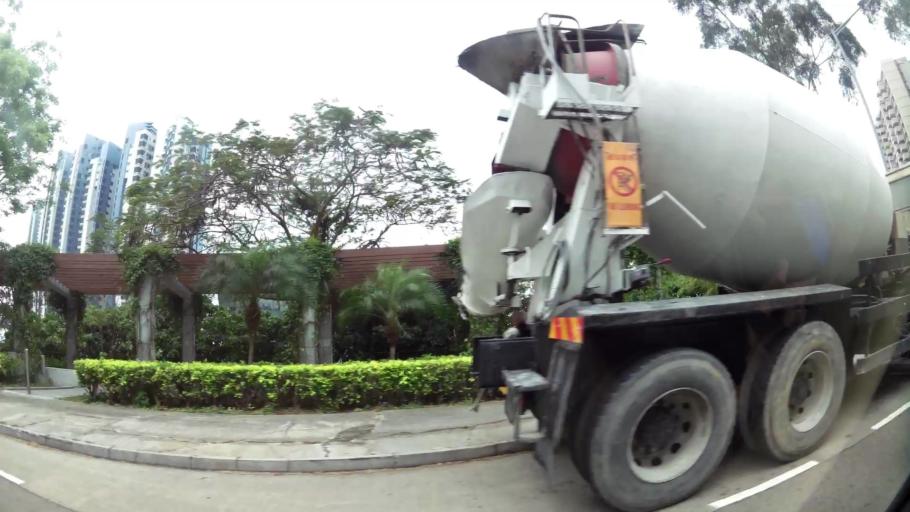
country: HK
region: Central and Western
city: Central
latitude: 22.2598
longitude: 114.1335
